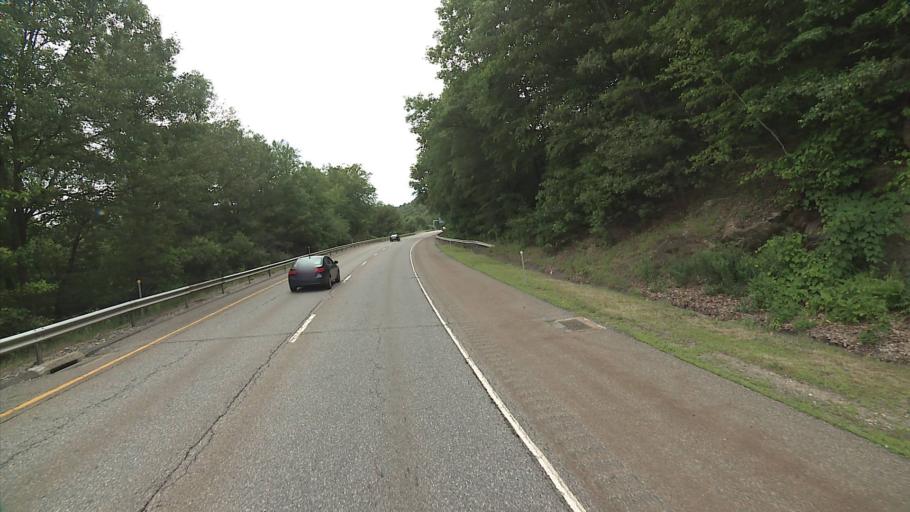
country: US
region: Connecticut
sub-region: Litchfield County
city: Thomaston
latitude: 41.6943
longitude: -73.0687
